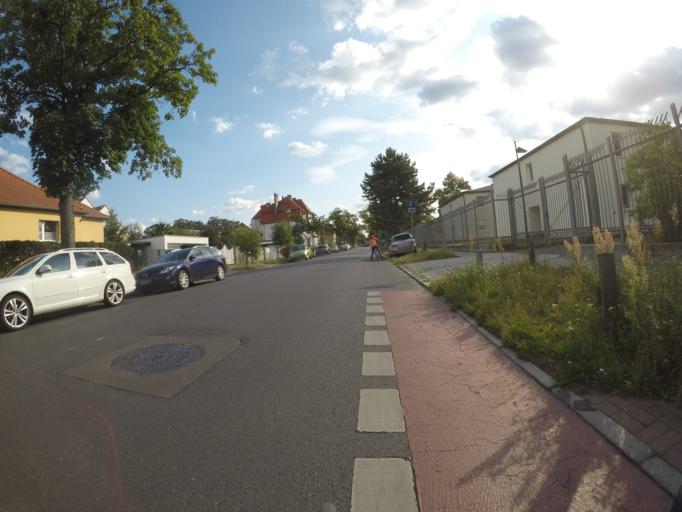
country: DE
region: Berlin
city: Kaulsdorf
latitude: 52.5153
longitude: 13.5928
